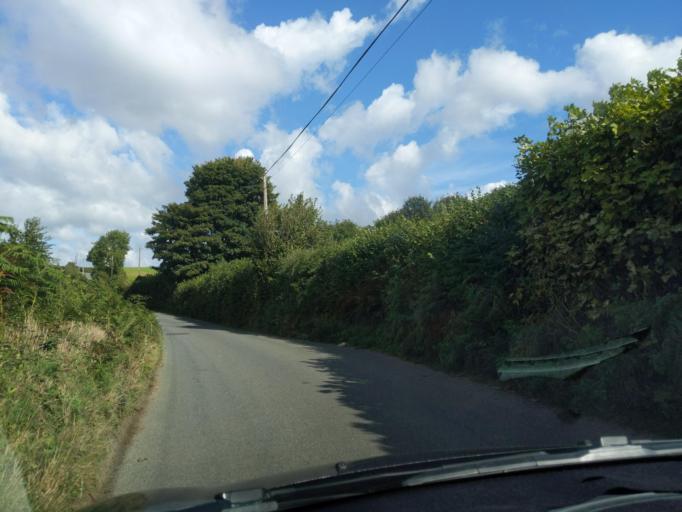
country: GB
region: England
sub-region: Devon
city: Great Torrington
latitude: 50.9398
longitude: -4.1754
